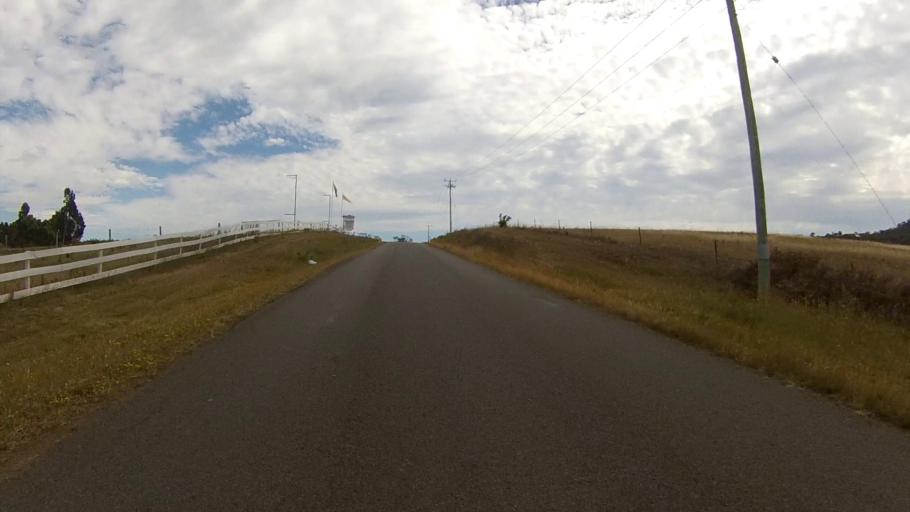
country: AU
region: Tasmania
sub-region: Clarence
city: Cambridge
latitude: -42.7280
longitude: 147.4493
